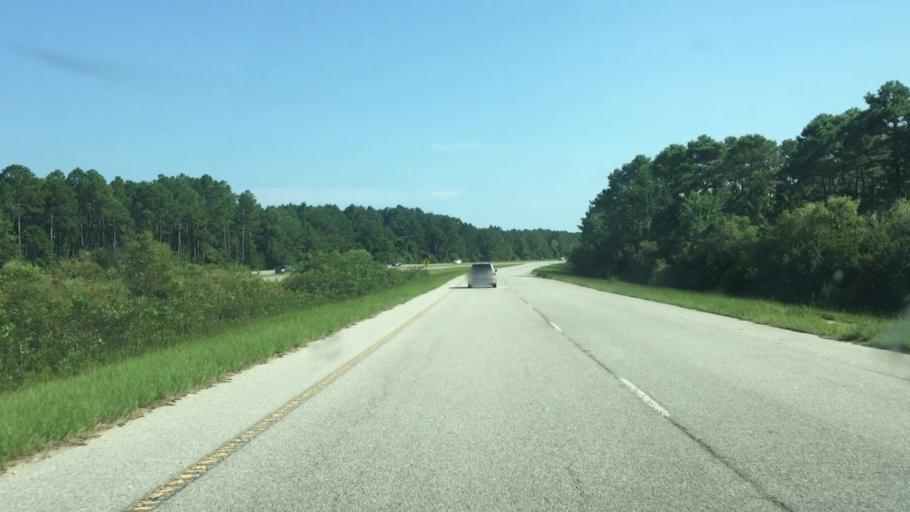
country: US
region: South Carolina
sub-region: Horry County
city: North Myrtle Beach
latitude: 33.8065
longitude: -78.7796
